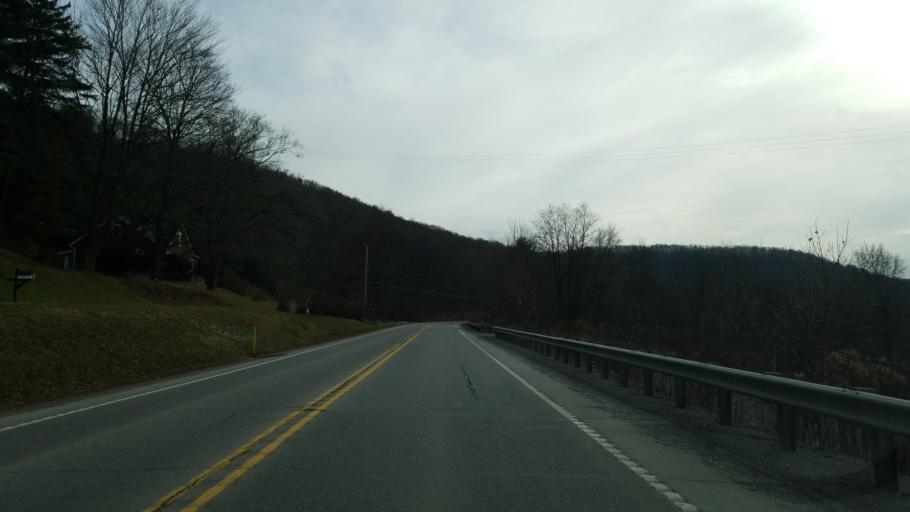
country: US
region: Pennsylvania
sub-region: Clearfield County
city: Clearfield
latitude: 41.0104
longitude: -78.3887
